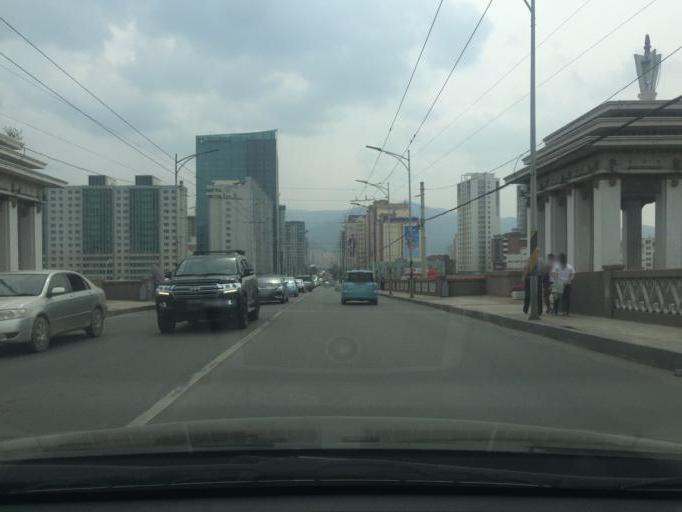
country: MN
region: Ulaanbaatar
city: Ulaanbaatar
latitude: 47.9078
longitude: 106.9130
